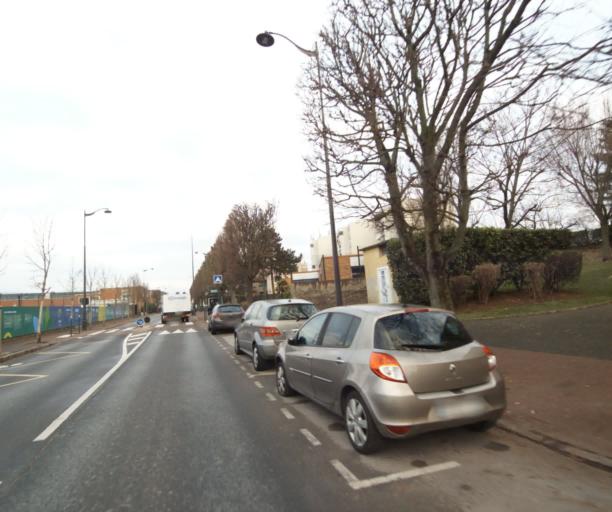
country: FR
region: Ile-de-France
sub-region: Departement des Hauts-de-Seine
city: Rueil-Malmaison
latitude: 48.8731
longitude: 2.2021
